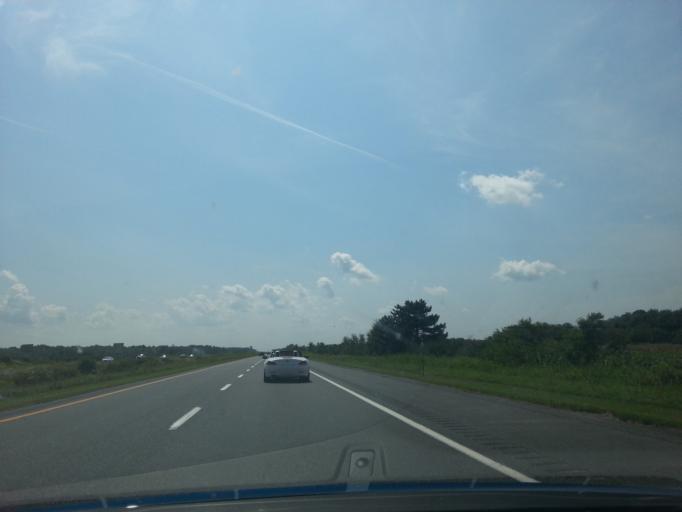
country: CA
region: Quebec
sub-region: Mauricie
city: Saint-Germain-de-Grantham
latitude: 45.8434
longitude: -72.5941
